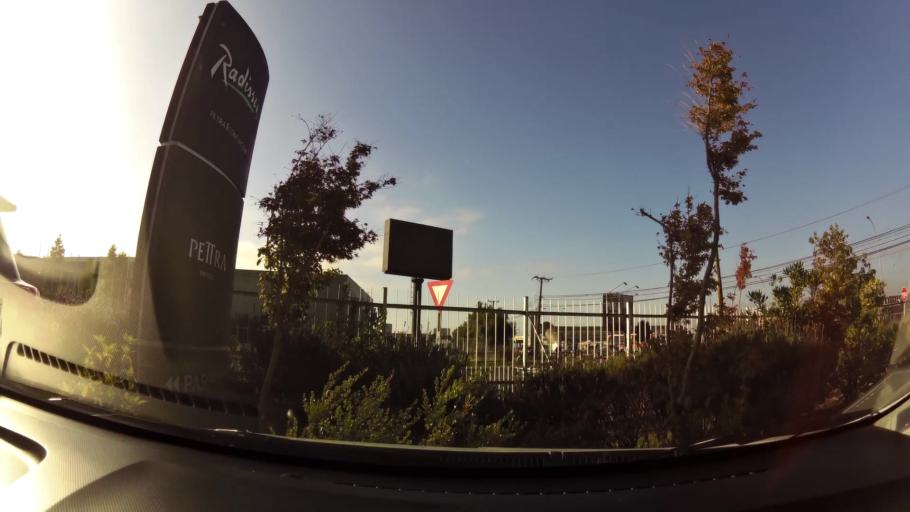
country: CL
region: Biobio
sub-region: Provincia de Concepcion
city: Concepcion
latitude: -36.7928
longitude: -73.0707
